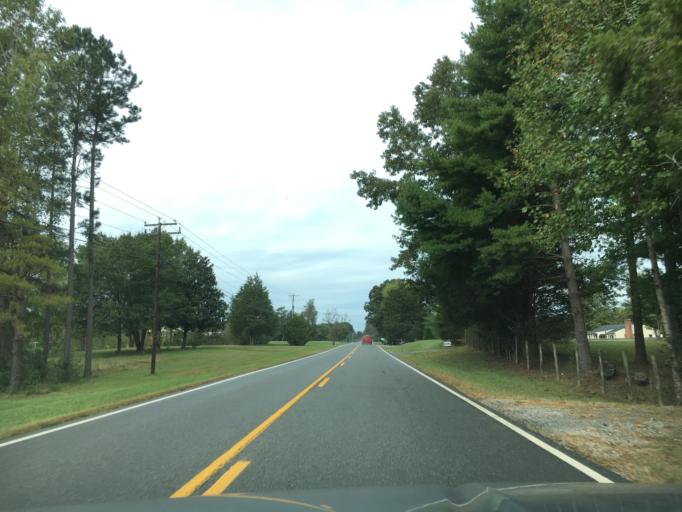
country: US
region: Virginia
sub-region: Goochland County
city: Goochland
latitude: 37.7245
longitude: -77.8305
